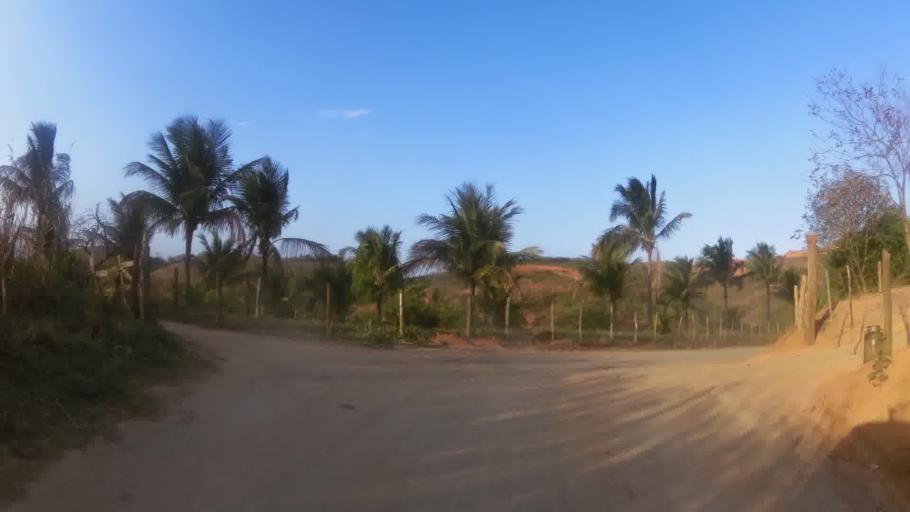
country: BR
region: Espirito Santo
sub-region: Piuma
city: Piuma
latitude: -20.8907
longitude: -40.8024
